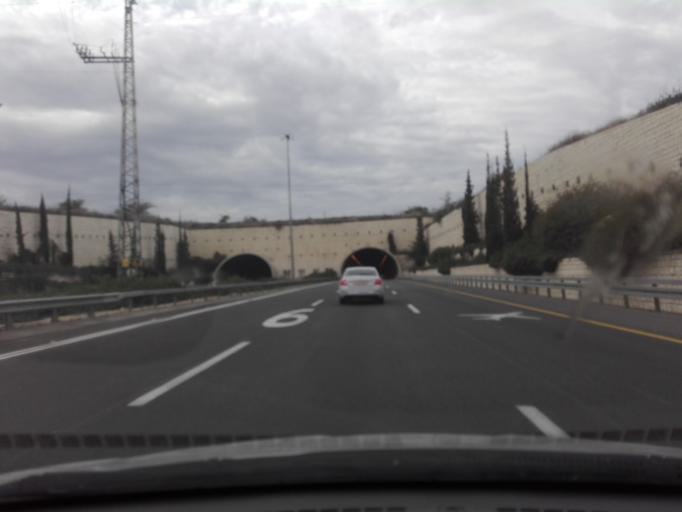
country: PS
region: West Bank
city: Budrus
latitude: 31.9679
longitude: 34.9539
